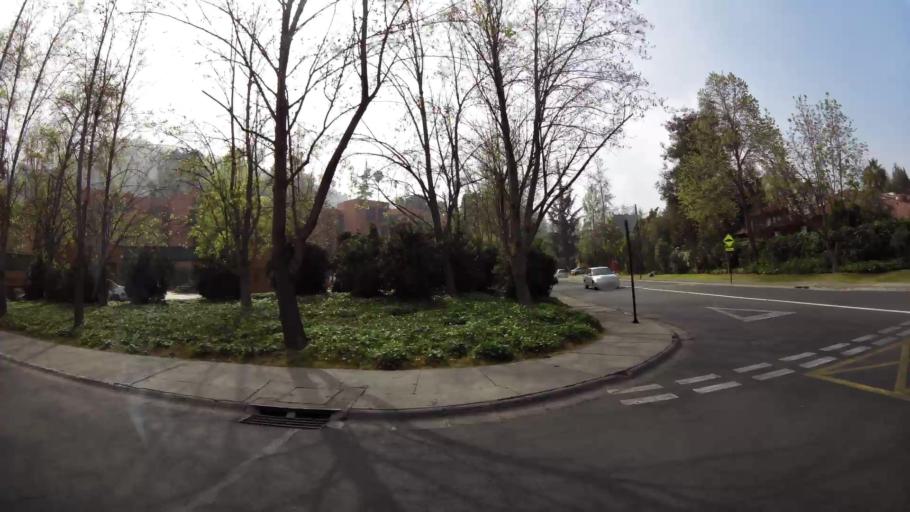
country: CL
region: Santiago Metropolitan
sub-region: Provincia de Santiago
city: Villa Presidente Frei, Nunoa, Santiago, Chile
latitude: -33.3741
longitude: -70.5708
